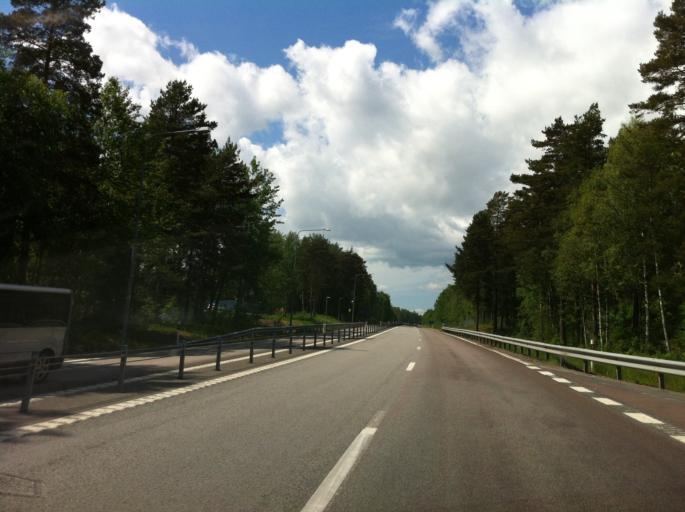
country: SE
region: Vaermland
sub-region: Saffle Kommun
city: Saeffle
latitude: 59.1356
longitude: 12.9127
